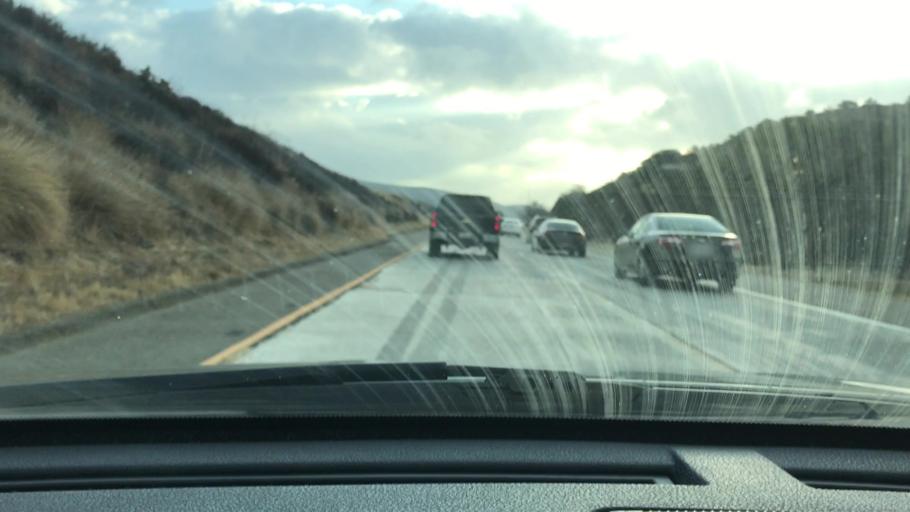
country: US
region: California
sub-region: Ventura County
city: Thousand Oaks
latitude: 34.1751
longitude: -118.8563
